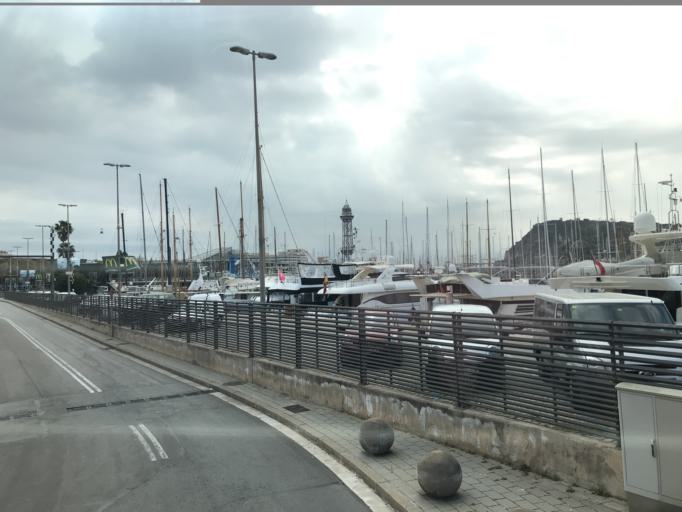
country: ES
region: Catalonia
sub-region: Provincia de Barcelona
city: Ciutat Vella
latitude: 41.3788
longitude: 2.1831
